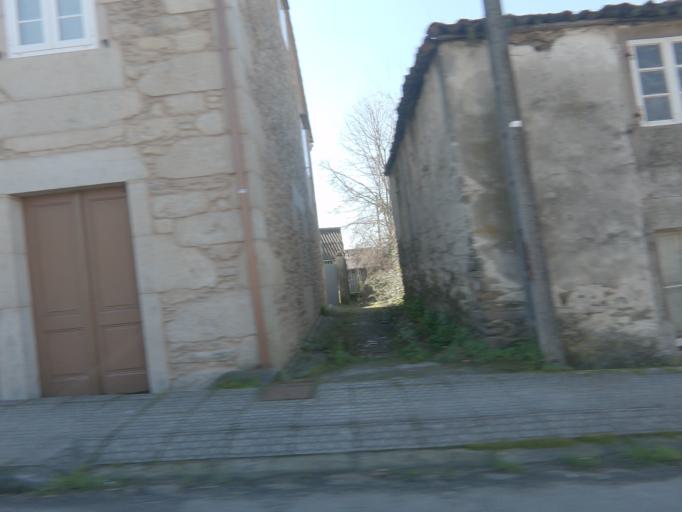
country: ES
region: Galicia
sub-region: Provincia de Pontevedra
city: Silleda
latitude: 42.6835
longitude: -8.1853
